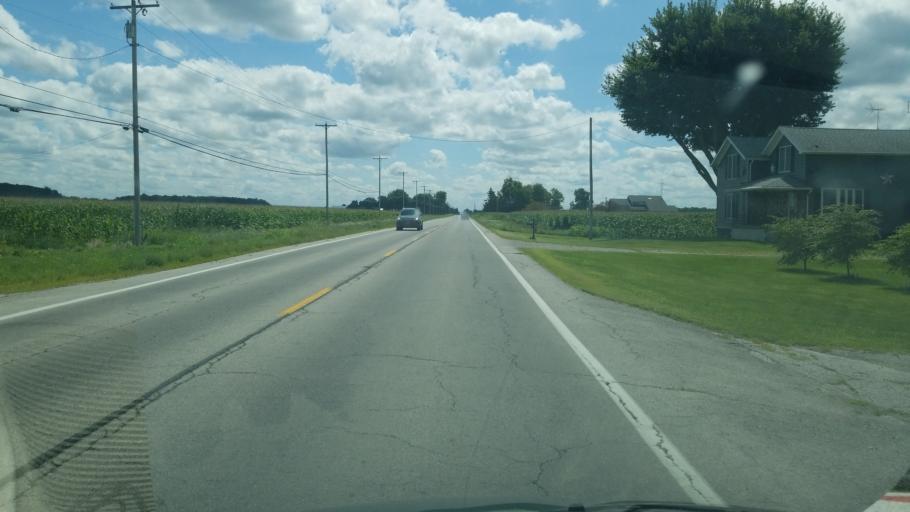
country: US
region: Ohio
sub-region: Henry County
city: Napoleon
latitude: 41.3674
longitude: -84.1203
